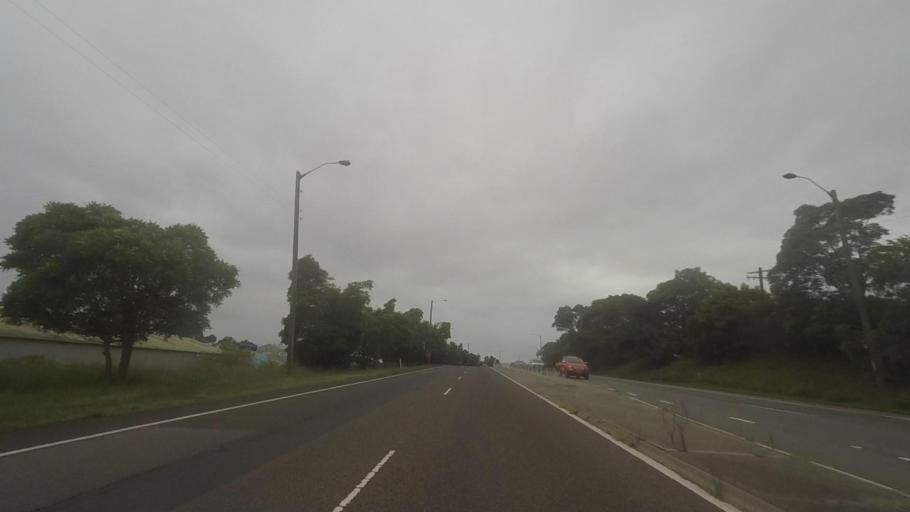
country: AU
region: New South Wales
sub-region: Newcastle
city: Mayfield
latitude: -32.8877
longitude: 151.7364
